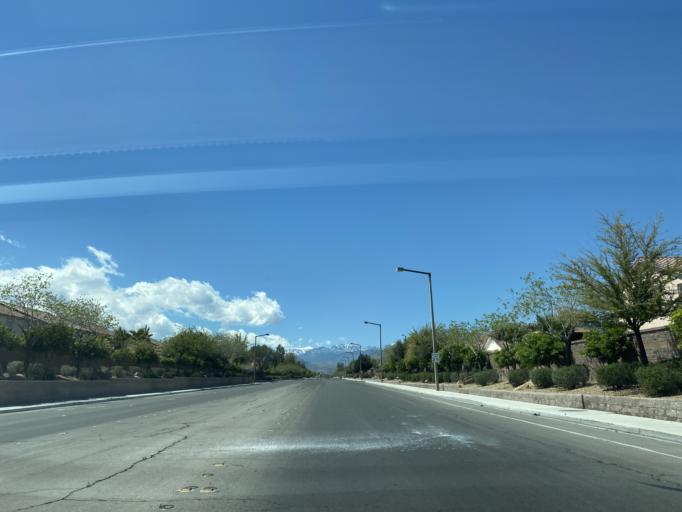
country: US
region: Nevada
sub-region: Clark County
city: North Las Vegas
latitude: 36.3134
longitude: -115.2076
